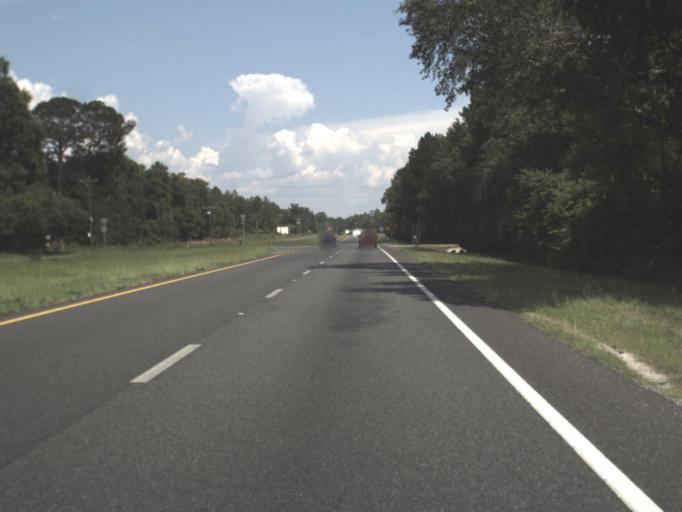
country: US
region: Florida
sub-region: Alachua County
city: Waldo
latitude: 29.7659
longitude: -82.1472
